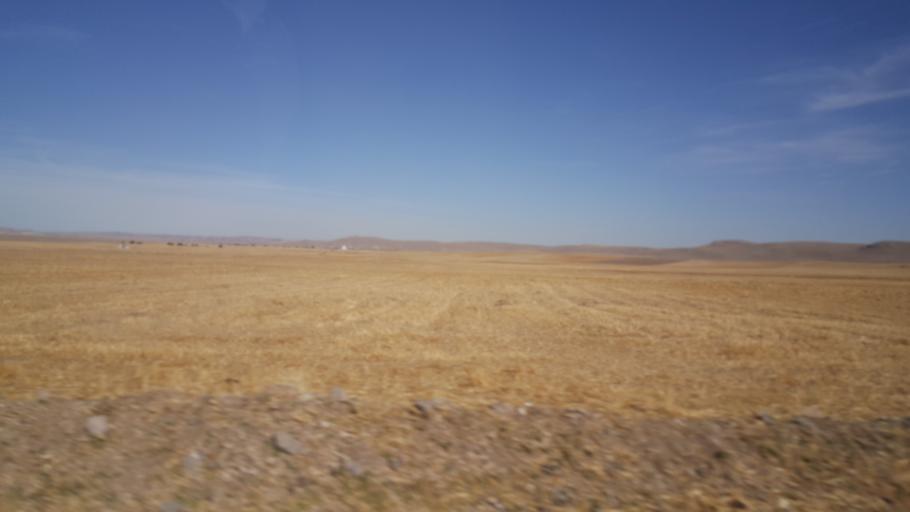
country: TR
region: Ankara
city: Yenice
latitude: 39.3334
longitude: 32.7506
